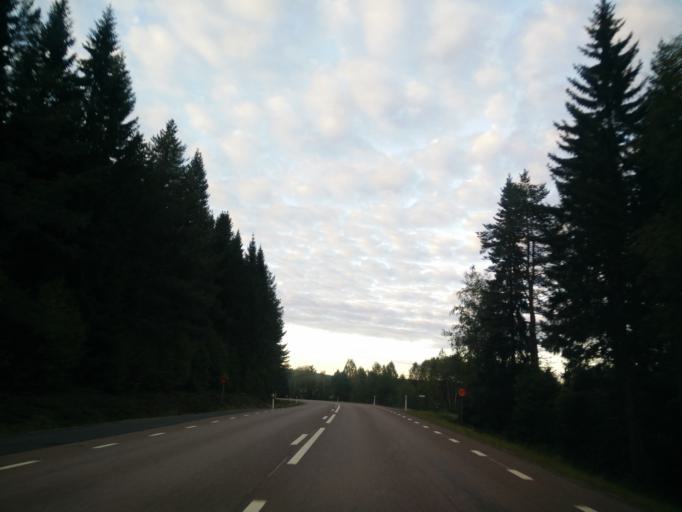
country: SE
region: Vaesternorrland
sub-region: Kramfors Kommun
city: Nordingra
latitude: 62.9225
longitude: 18.0749
